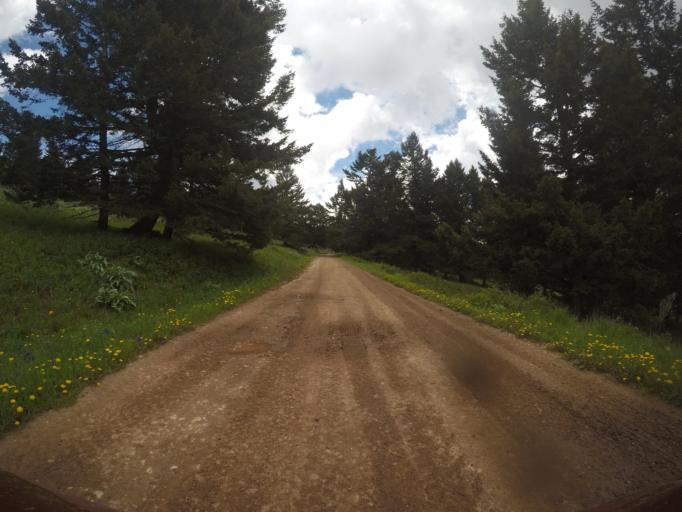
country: US
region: Wyoming
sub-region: Big Horn County
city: Lovell
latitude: 45.1716
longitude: -108.4323
